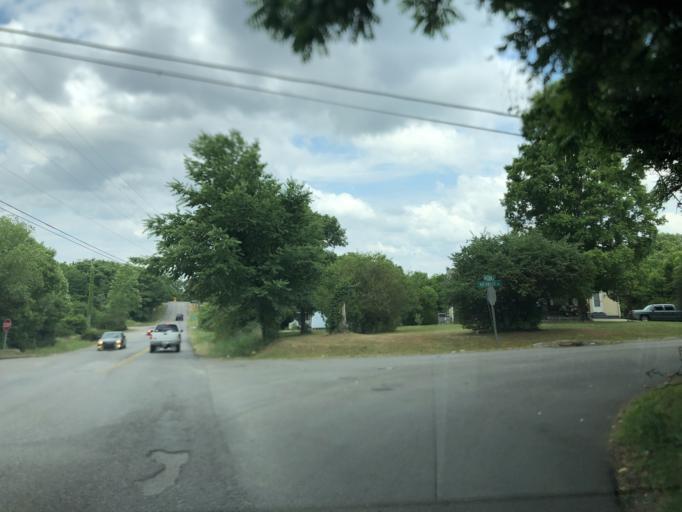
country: US
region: Tennessee
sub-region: Davidson County
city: Goodlettsville
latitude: 36.2720
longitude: -86.6877
